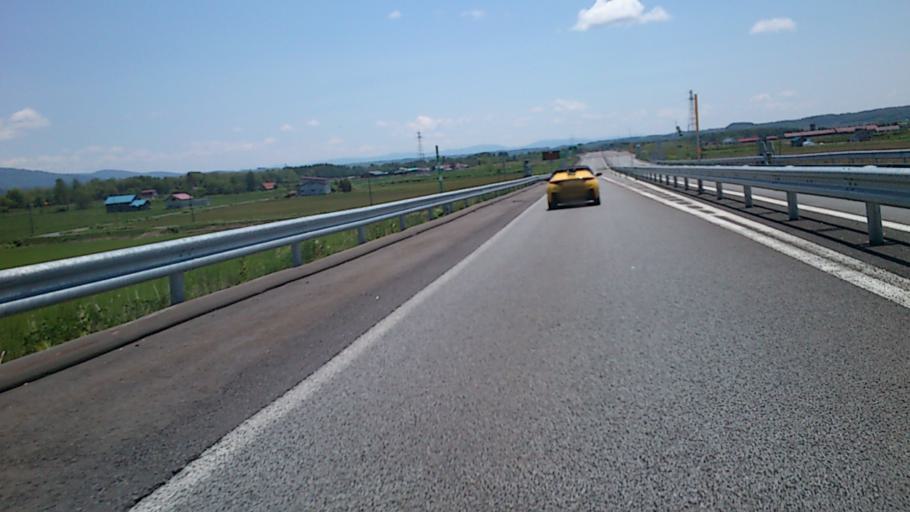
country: JP
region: Hokkaido
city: Nayoro
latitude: 44.4813
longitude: 142.3670
